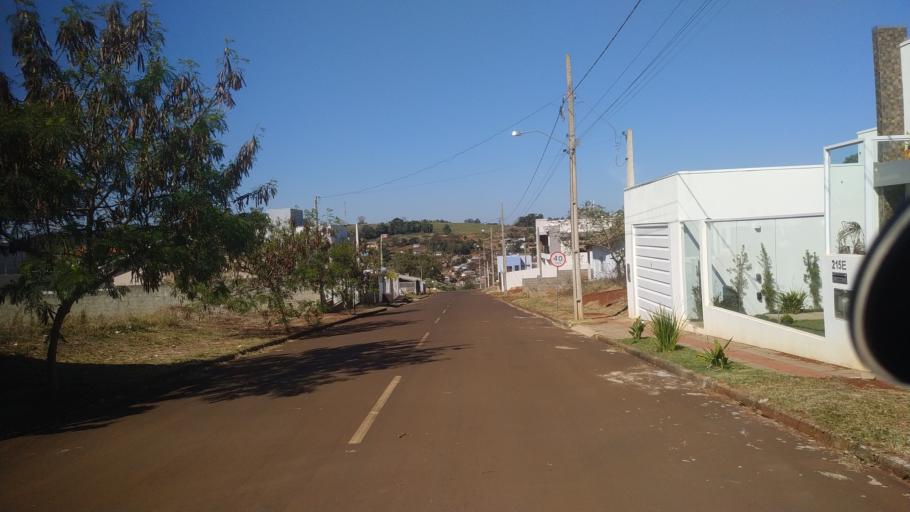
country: BR
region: Santa Catarina
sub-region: Chapeco
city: Chapeco
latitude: -27.0901
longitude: -52.5804
